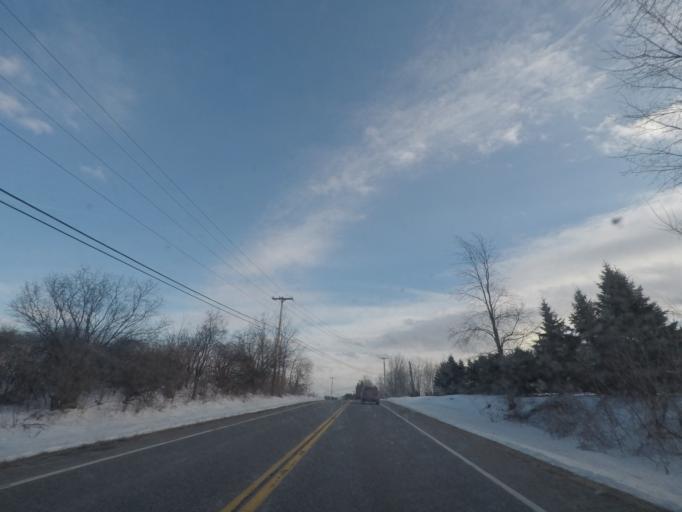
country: US
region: New York
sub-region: Schenectady County
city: Niskayuna
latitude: 42.8395
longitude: -73.8583
